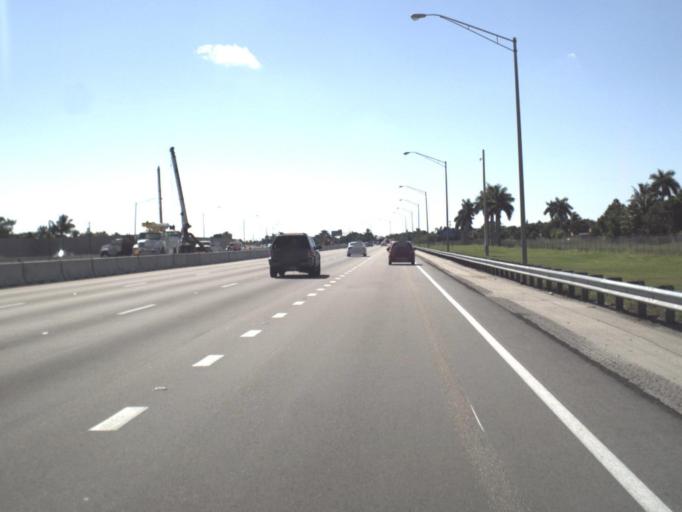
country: US
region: Florida
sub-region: Miami-Dade County
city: South Miami Heights
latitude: 25.6078
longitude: -80.3784
